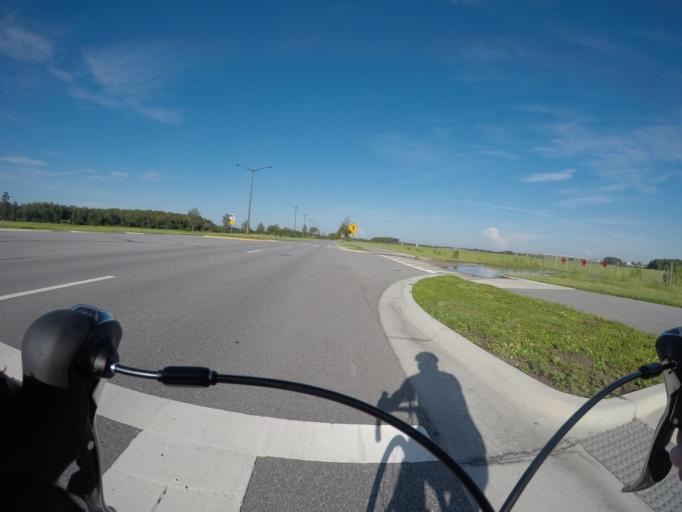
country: US
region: Florida
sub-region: Osceola County
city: Buenaventura Lakes
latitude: 28.3675
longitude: -81.2921
